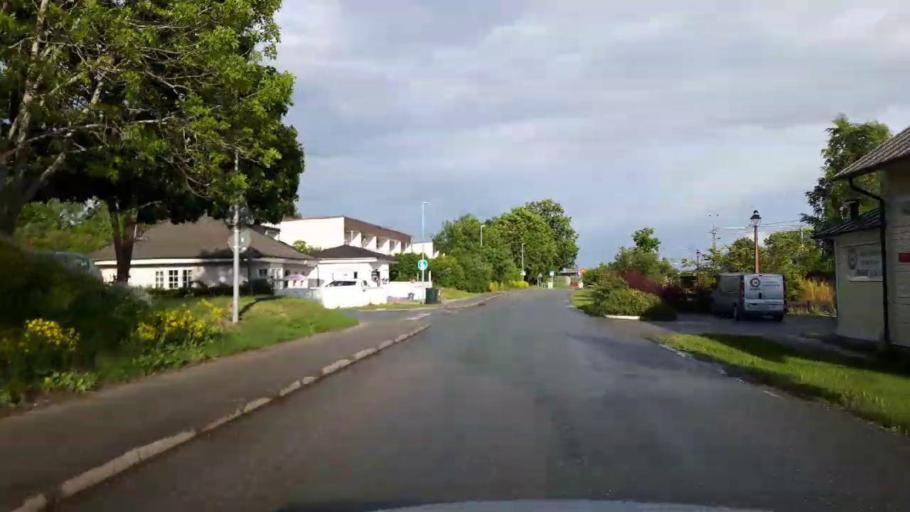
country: SE
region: Stockholm
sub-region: Upplands-Bro Kommun
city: Bro
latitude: 59.5104
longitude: 17.6407
